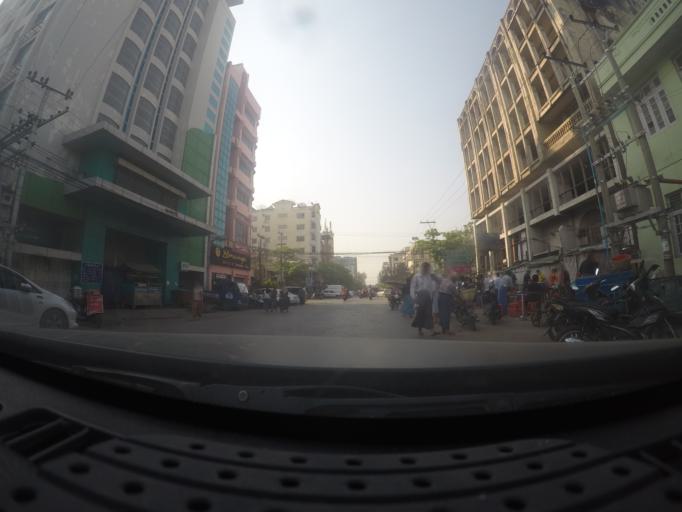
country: MM
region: Mandalay
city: Mandalay
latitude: 21.9807
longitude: 96.0810
